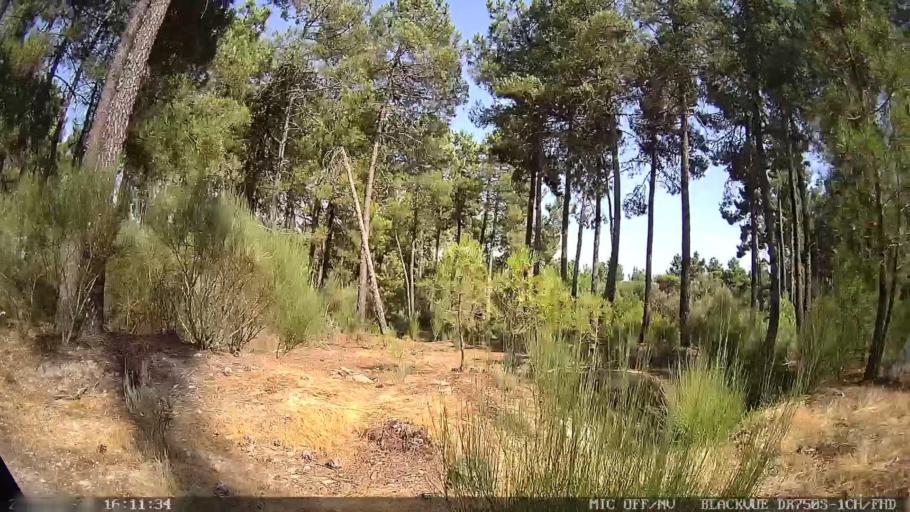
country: PT
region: Vila Real
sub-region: Murca
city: Murca
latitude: 41.3441
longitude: -7.4740
